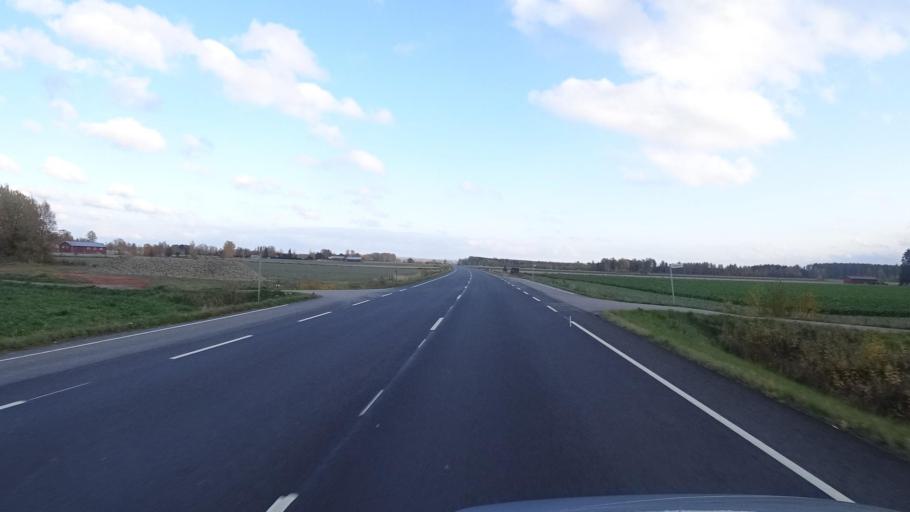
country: FI
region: Satakunta
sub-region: Rauma
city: Koeylioe
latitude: 61.0781
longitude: 22.2825
